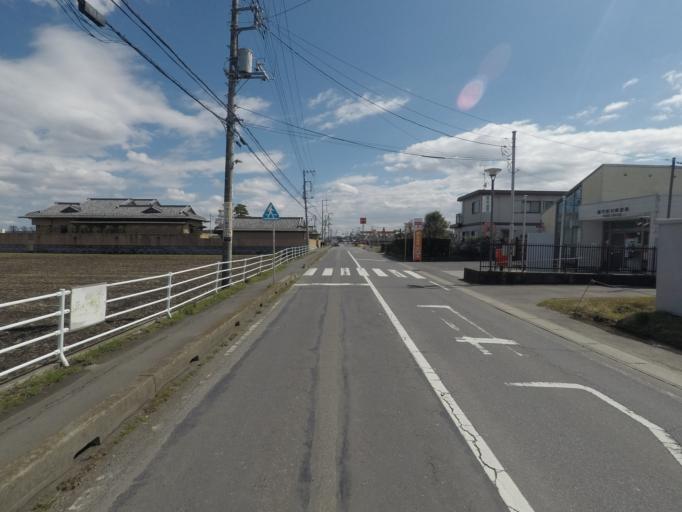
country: JP
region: Ibaraki
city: Fujishiro
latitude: 35.9353
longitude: 140.1249
